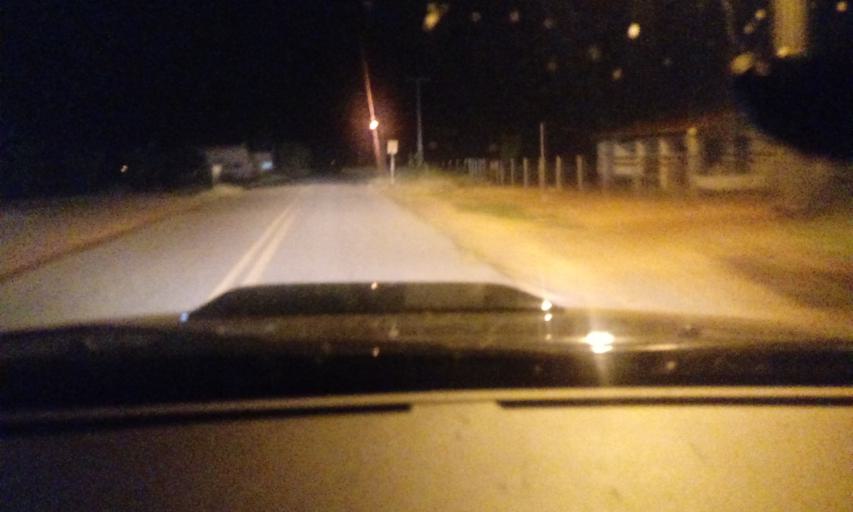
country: BR
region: Bahia
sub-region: Guanambi
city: Guanambi
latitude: -14.1140
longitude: -42.8615
